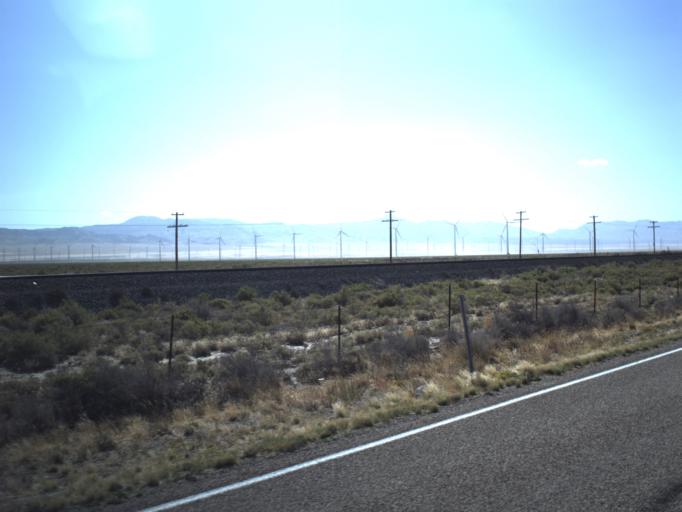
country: US
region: Utah
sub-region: Beaver County
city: Milford
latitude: 38.6119
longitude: -112.9859
